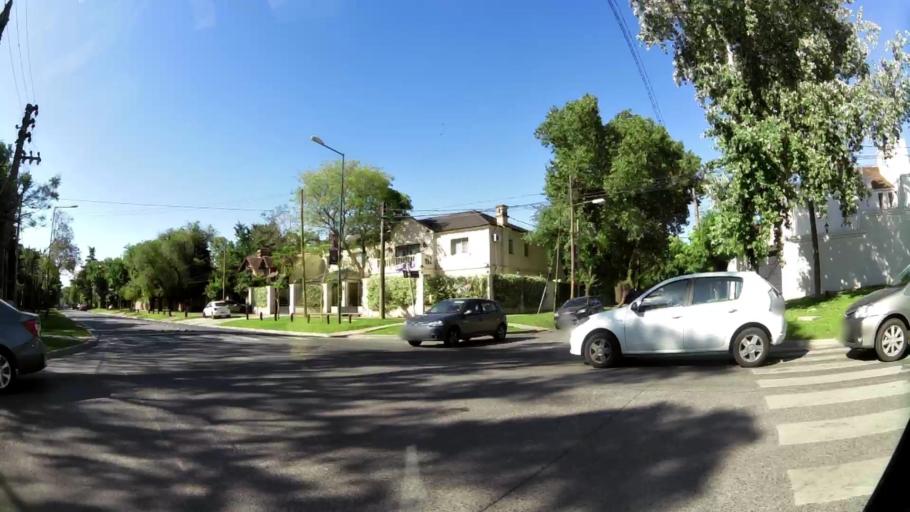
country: AR
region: Buenos Aires
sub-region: Partido de San Isidro
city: San Isidro
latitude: -34.4853
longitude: -58.5507
